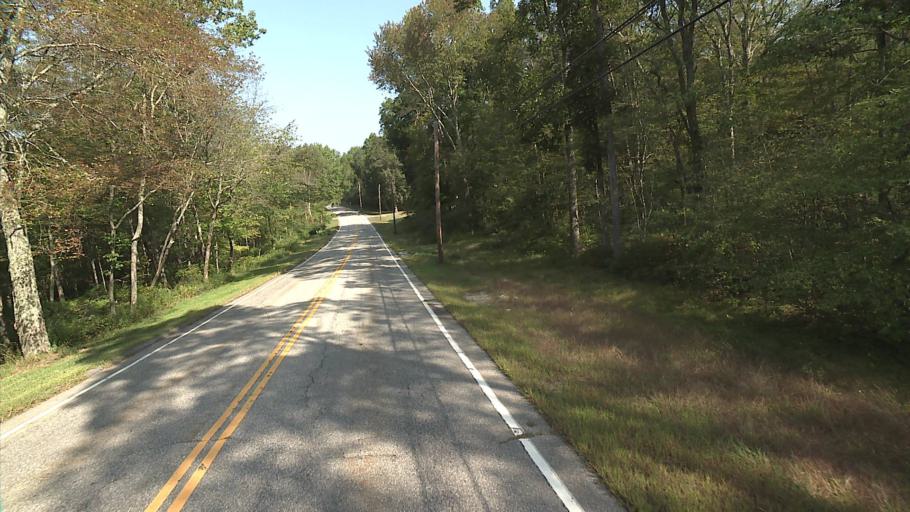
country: US
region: Connecticut
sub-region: Windham County
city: Plainfield Village
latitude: 41.6868
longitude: -71.9675
